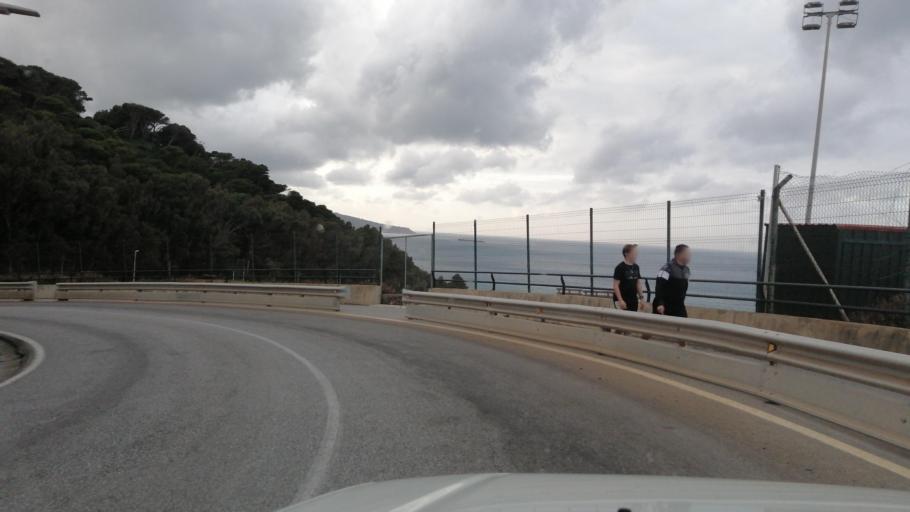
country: ES
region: Ceuta
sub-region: Ceuta
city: Ceuta
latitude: 35.9018
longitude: -5.2870
